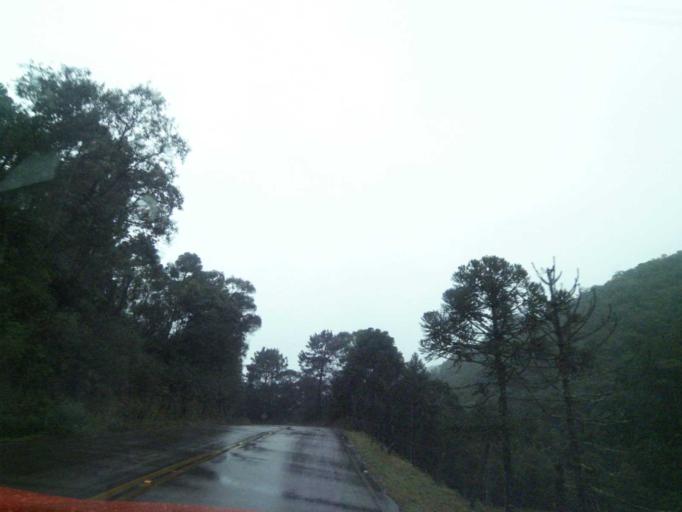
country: BR
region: Santa Catarina
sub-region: Anitapolis
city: Anitapolis
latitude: -27.7942
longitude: -49.0444
